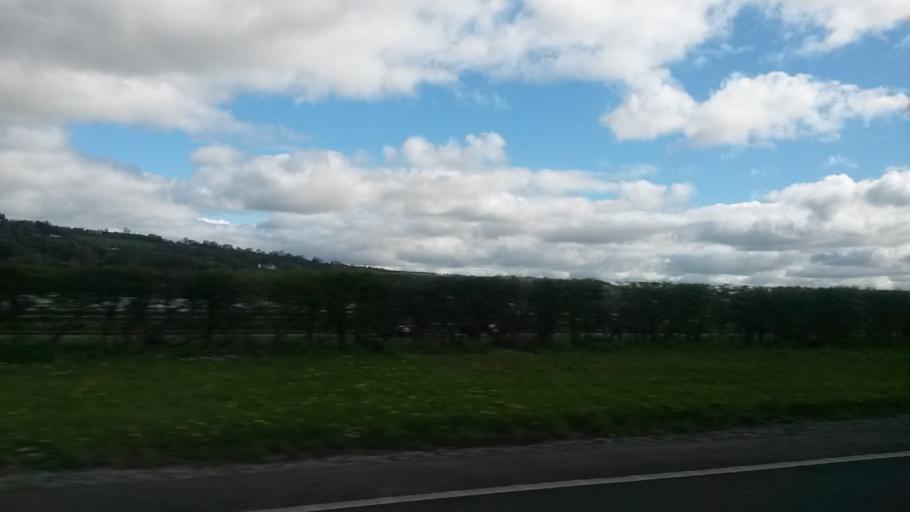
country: IE
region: Munster
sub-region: County Cork
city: Passage West
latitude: 51.9055
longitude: -8.3222
